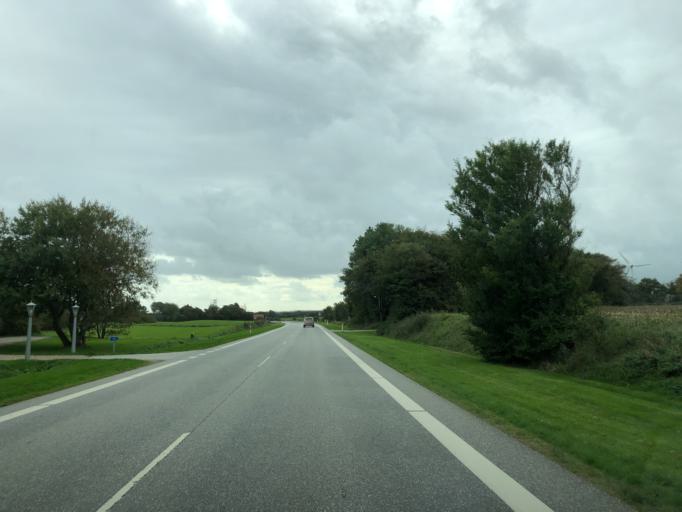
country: DK
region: North Denmark
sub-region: Thisted Kommune
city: Hurup
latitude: 56.8359
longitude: 8.5107
